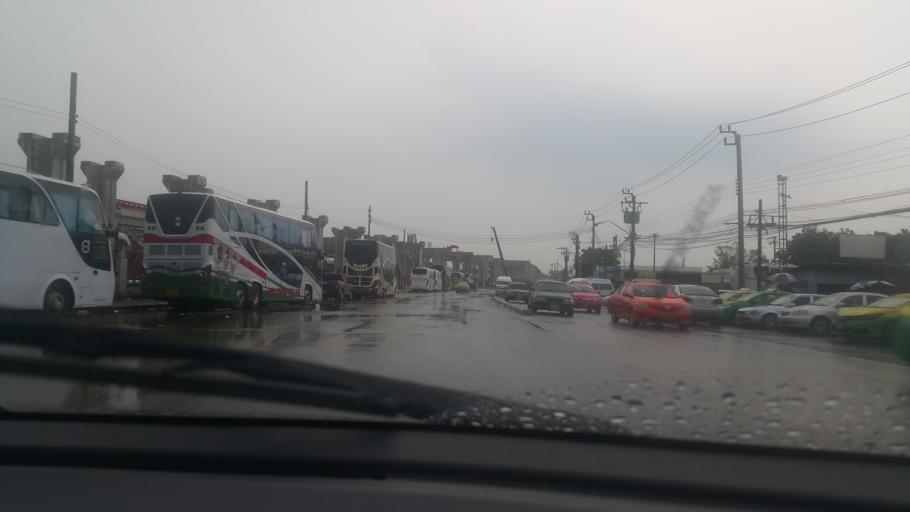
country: TH
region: Bangkok
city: Bang Sue
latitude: 13.8132
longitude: 100.5458
